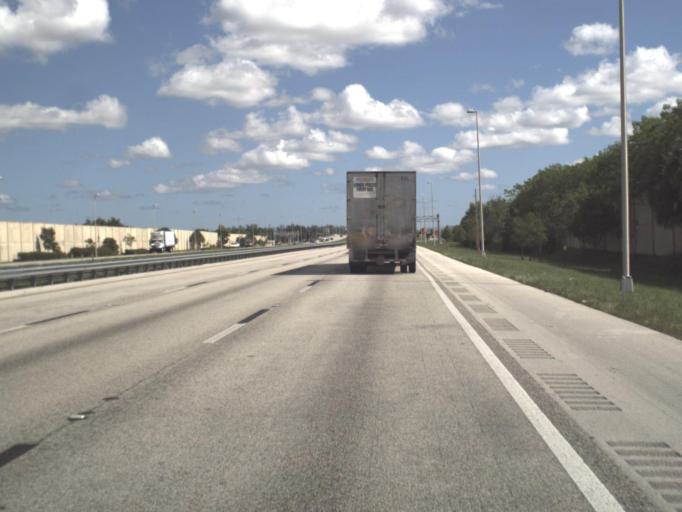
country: US
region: Florida
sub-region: Broward County
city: Parkland
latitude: 26.3018
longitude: -80.2607
